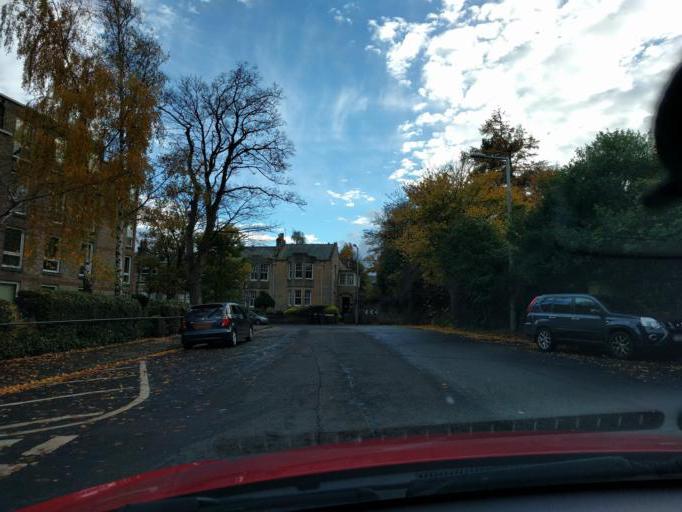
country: GB
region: Scotland
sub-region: Edinburgh
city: Colinton
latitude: 55.9225
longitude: -3.2236
